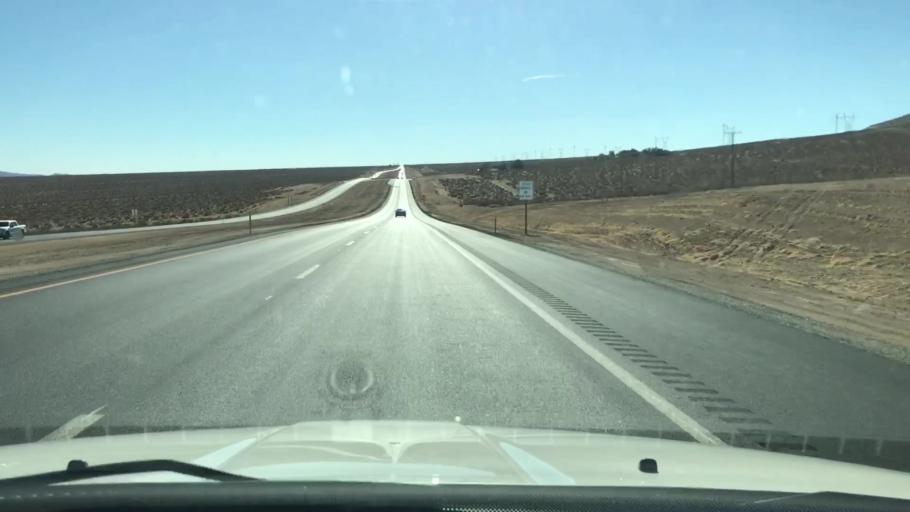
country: US
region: California
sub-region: Kern County
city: Inyokern
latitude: 35.6261
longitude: -117.8887
